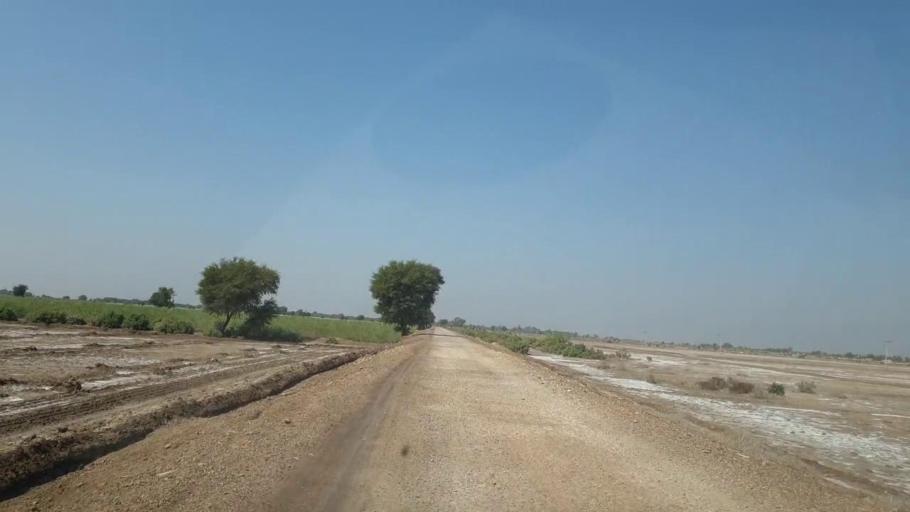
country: PK
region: Sindh
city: Mirpur Khas
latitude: 25.6936
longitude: 69.1096
